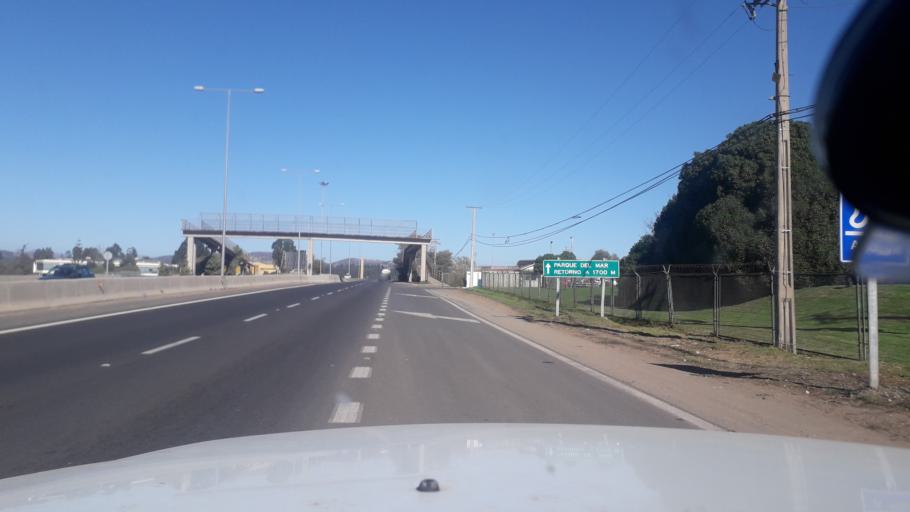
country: CL
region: Valparaiso
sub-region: Provincia de Valparaiso
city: Vina del Mar
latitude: -32.9584
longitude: -71.5102
